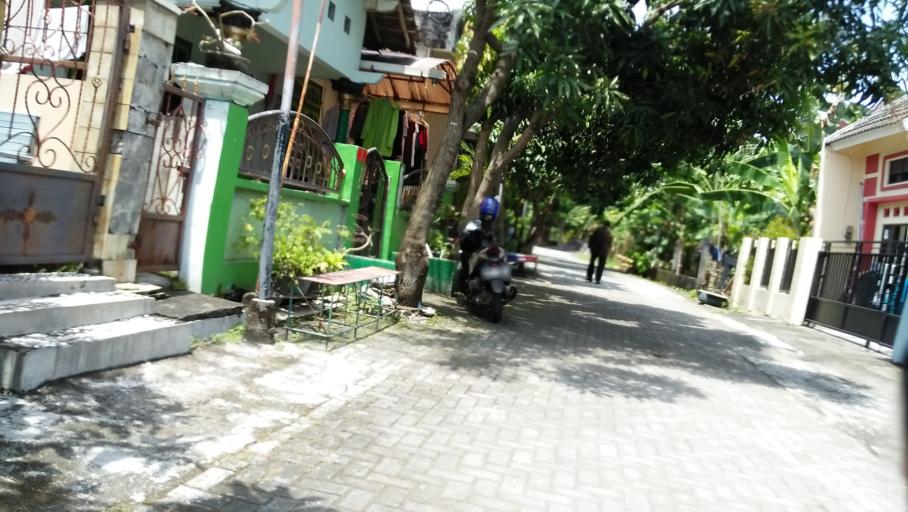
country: ID
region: Central Java
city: Mranggen
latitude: -7.0344
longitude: 110.4609
